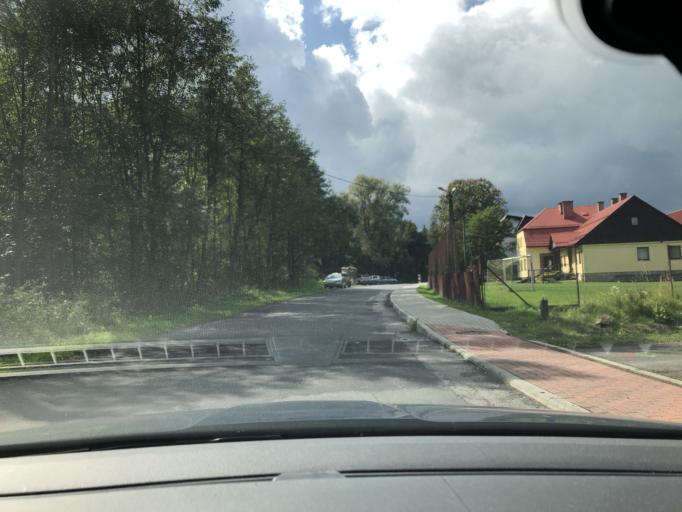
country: PL
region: Lesser Poland Voivodeship
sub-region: Powiat suski
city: Lachowice
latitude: 49.7087
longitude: 19.4304
